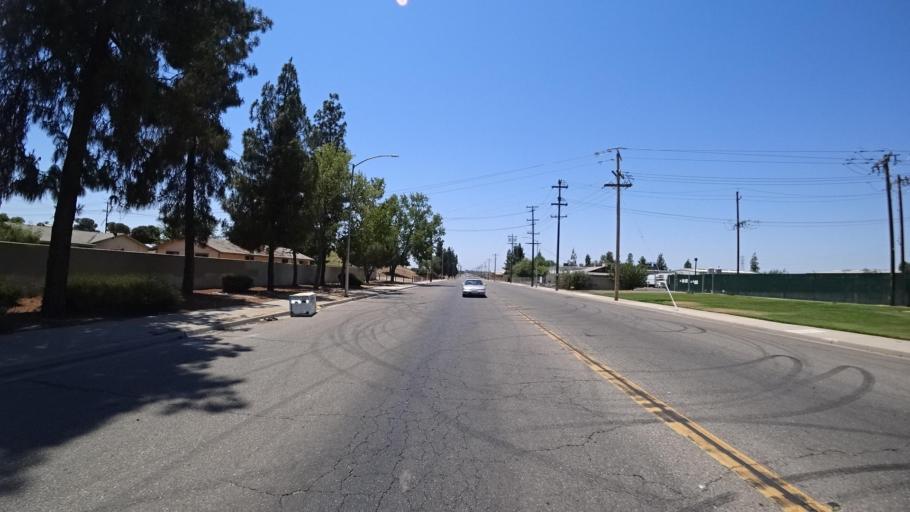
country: US
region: California
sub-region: Fresno County
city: West Park
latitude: 36.7183
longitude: -119.8178
